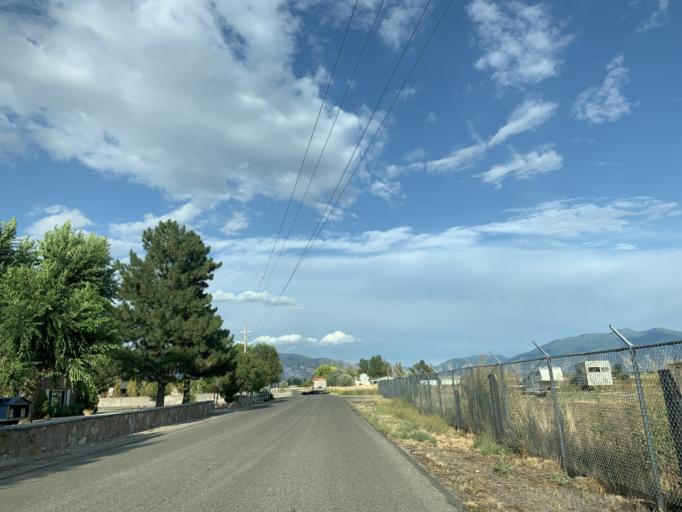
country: US
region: Utah
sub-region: Utah County
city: Benjamin
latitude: 40.1146
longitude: -111.7794
